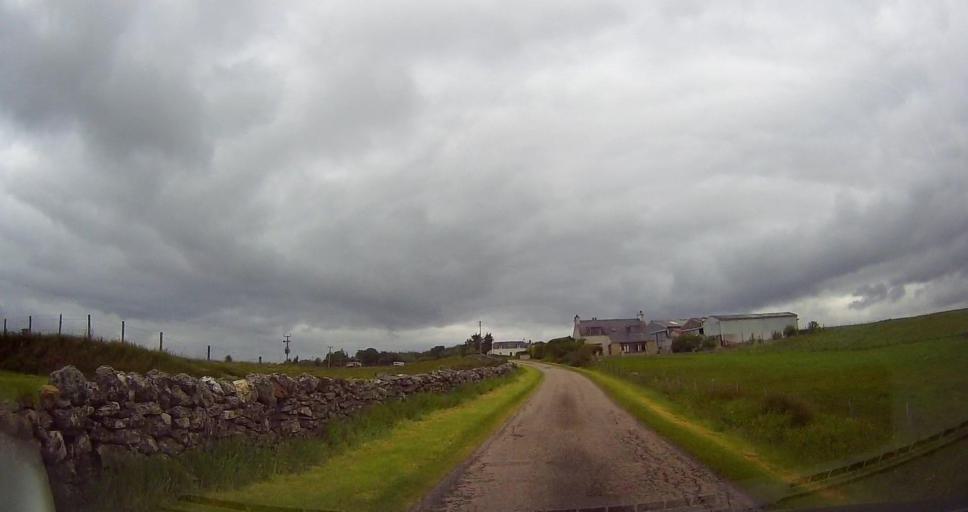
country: GB
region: Scotland
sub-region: Highland
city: Alness
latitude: 58.0773
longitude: -4.4441
